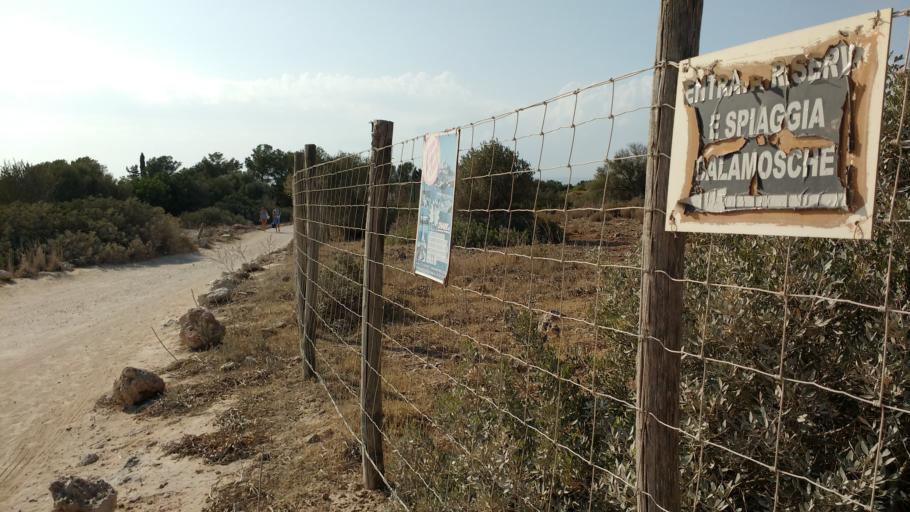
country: IT
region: Sicily
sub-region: Provincia di Siracusa
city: Noto
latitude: 36.8171
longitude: 15.0988
